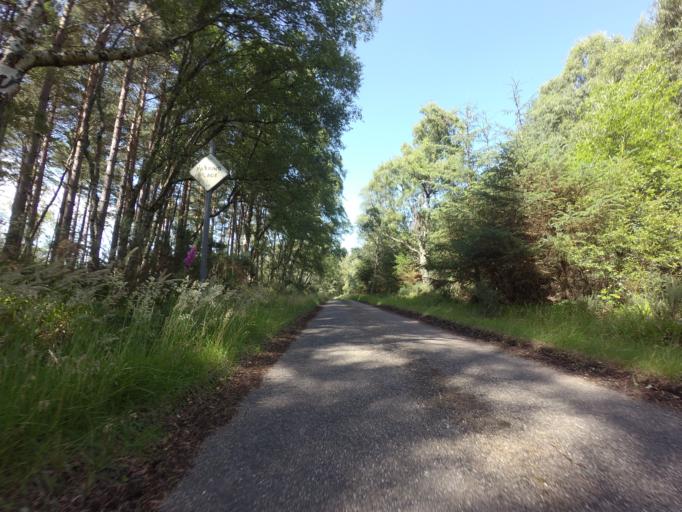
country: GB
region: Scotland
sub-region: Highland
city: Nairn
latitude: 57.5040
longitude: -3.9153
